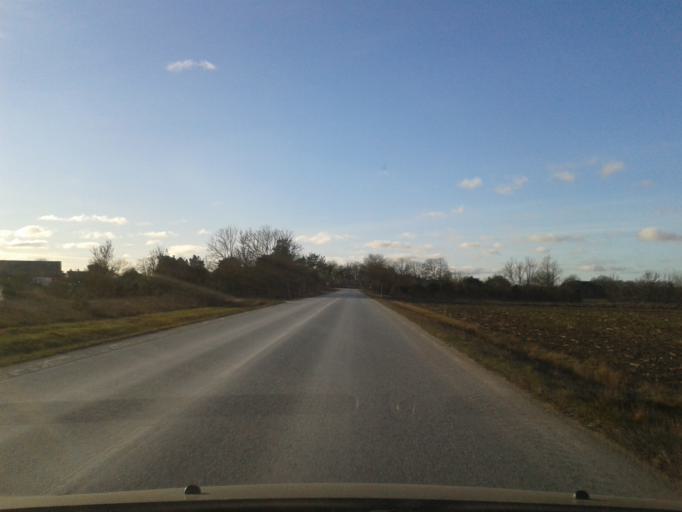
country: SE
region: Gotland
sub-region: Gotland
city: Slite
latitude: 57.4308
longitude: 18.6350
